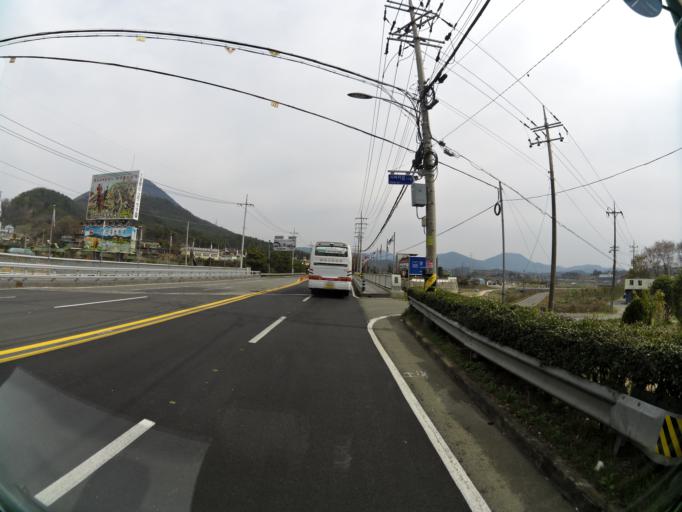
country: KR
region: Gyeongsangnam-do
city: Changnyeong
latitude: 35.4512
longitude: 128.5270
